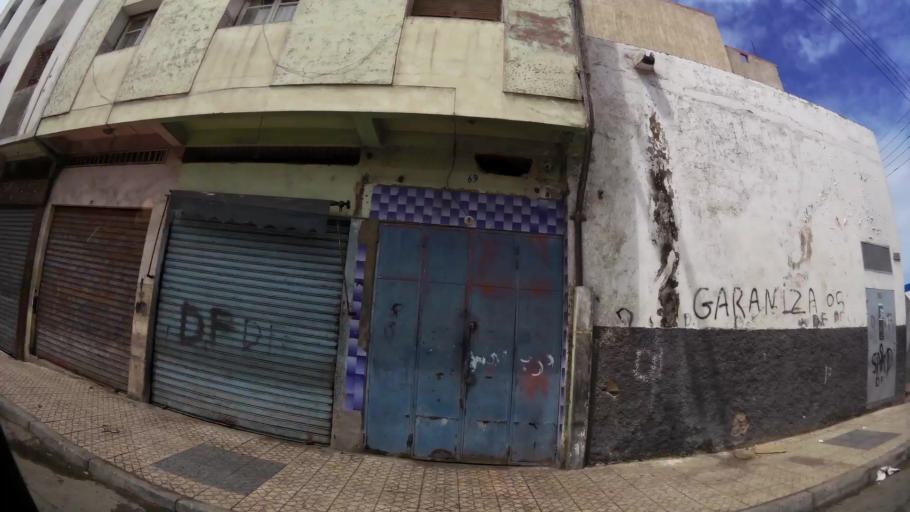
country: MA
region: Grand Casablanca
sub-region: Casablanca
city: Casablanca
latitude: 33.5731
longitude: -7.5886
